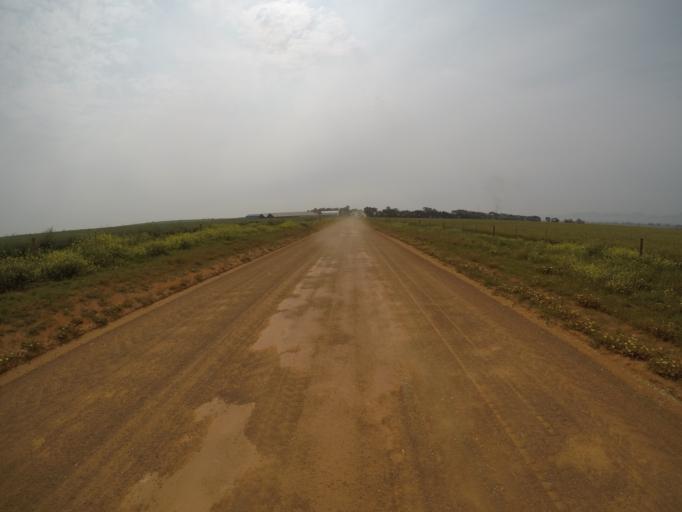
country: ZA
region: Western Cape
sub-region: City of Cape Town
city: Kraaifontein
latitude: -33.7091
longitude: 18.6888
